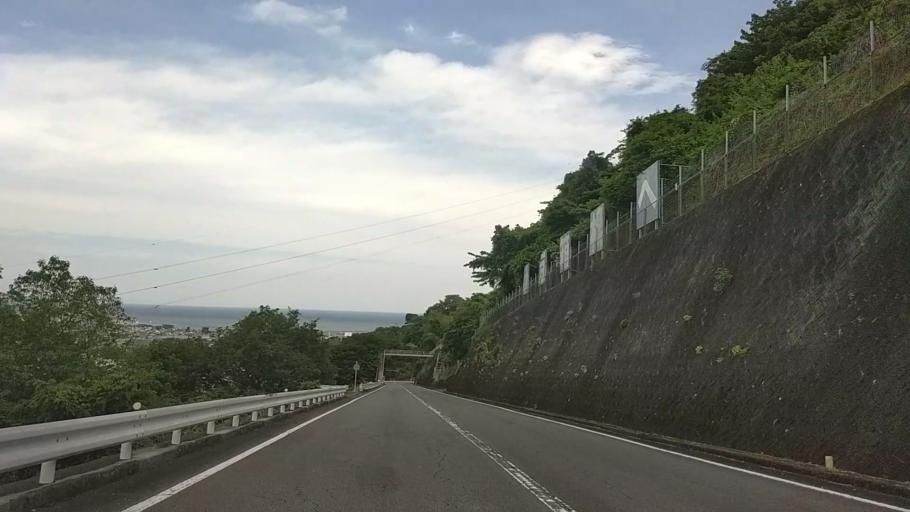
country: JP
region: Kanagawa
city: Odawara
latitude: 35.2432
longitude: 139.1344
